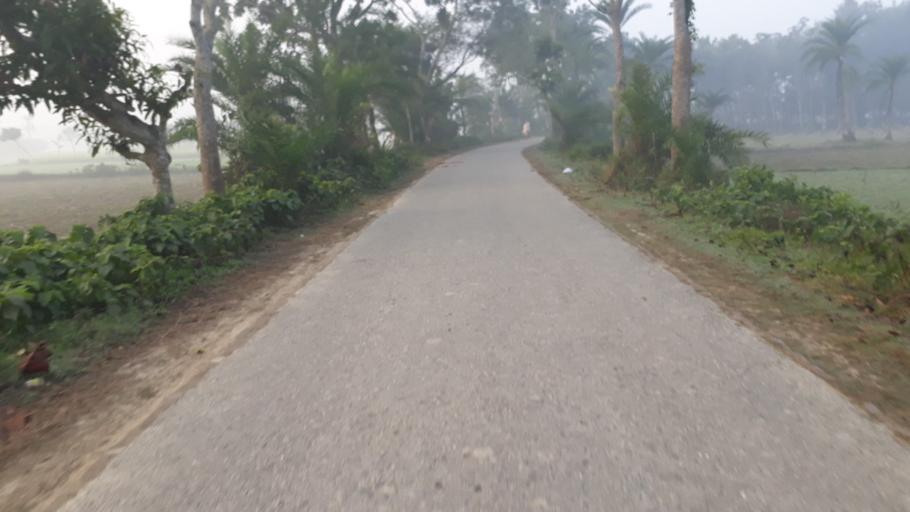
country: BD
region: Khulna
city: Jhingergacha
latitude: 23.2632
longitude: 88.9343
